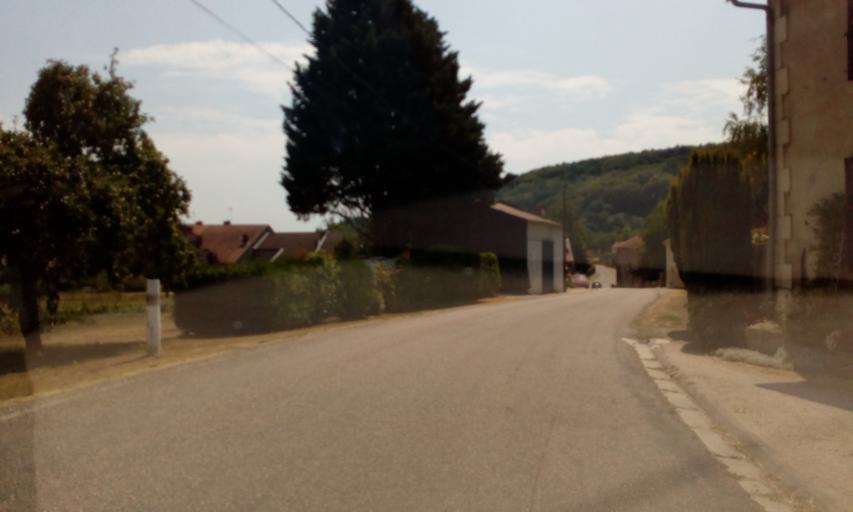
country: FR
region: Lorraine
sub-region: Departement de la Meuse
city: Etain
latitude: 49.1309
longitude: 5.5522
